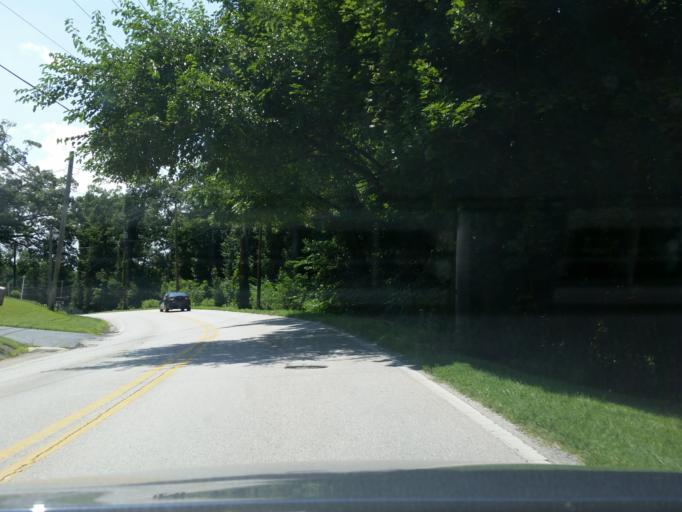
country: US
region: Pennsylvania
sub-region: York County
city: Shiloh
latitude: 39.9830
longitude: -76.7957
